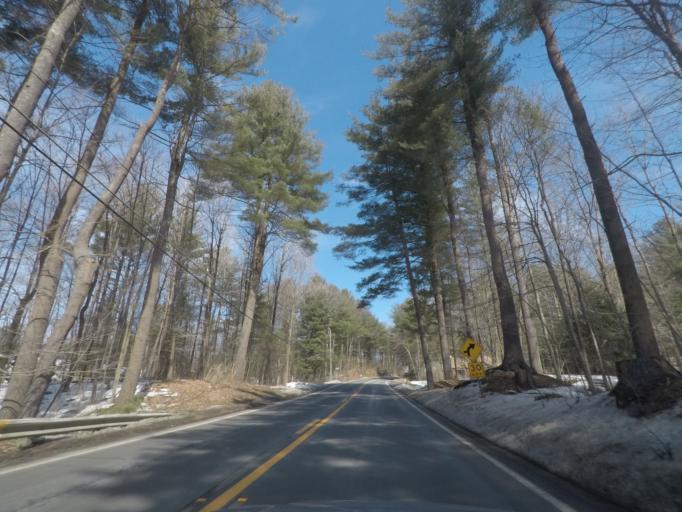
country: US
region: Massachusetts
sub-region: Berkshire County
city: Richmond
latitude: 42.3644
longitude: -73.3789
